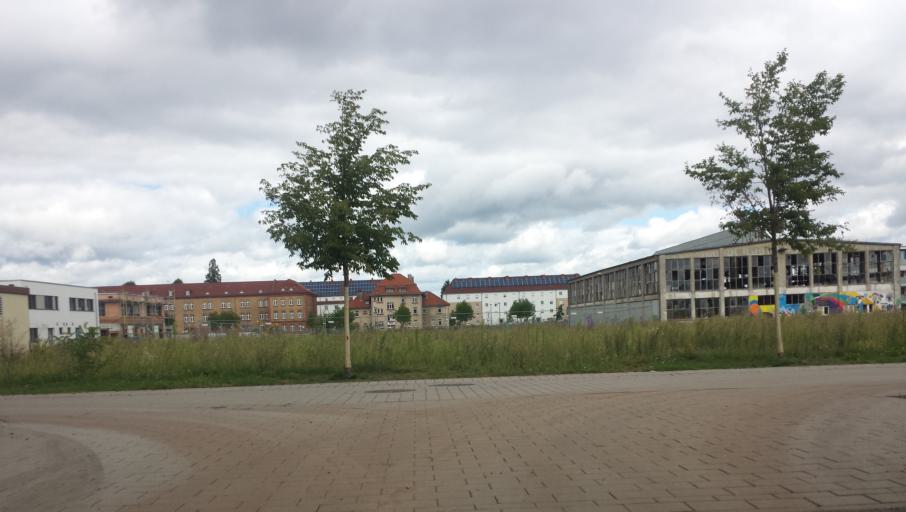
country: DE
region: Rheinland-Pfalz
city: Landau in der Pfalz
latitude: 49.1885
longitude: 8.1230
